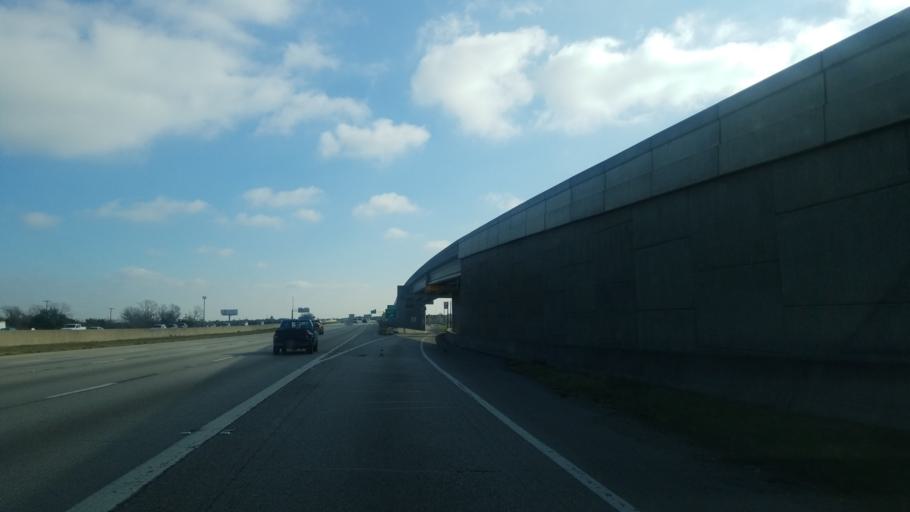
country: US
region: Texas
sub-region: Dallas County
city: DeSoto
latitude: 32.6422
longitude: -96.8123
